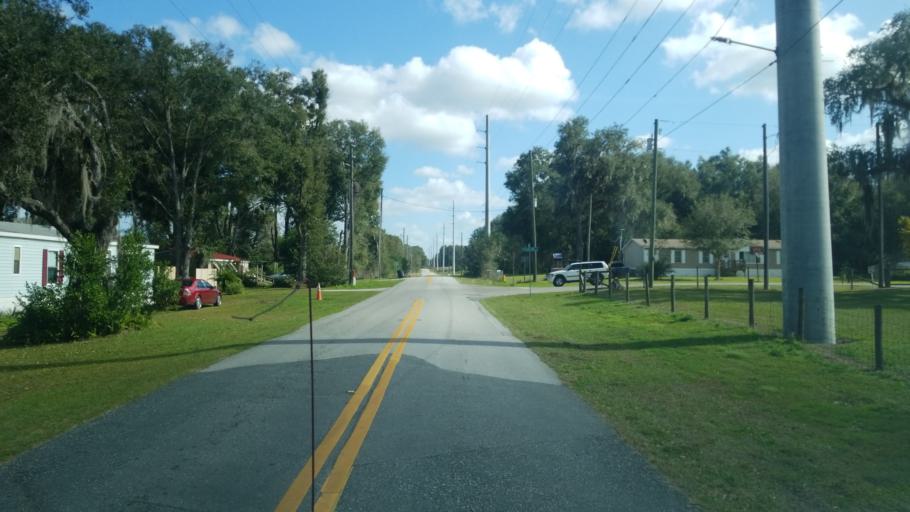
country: US
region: Florida
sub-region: Citrus County
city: Floral City
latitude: 28.7247
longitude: -82.3041
